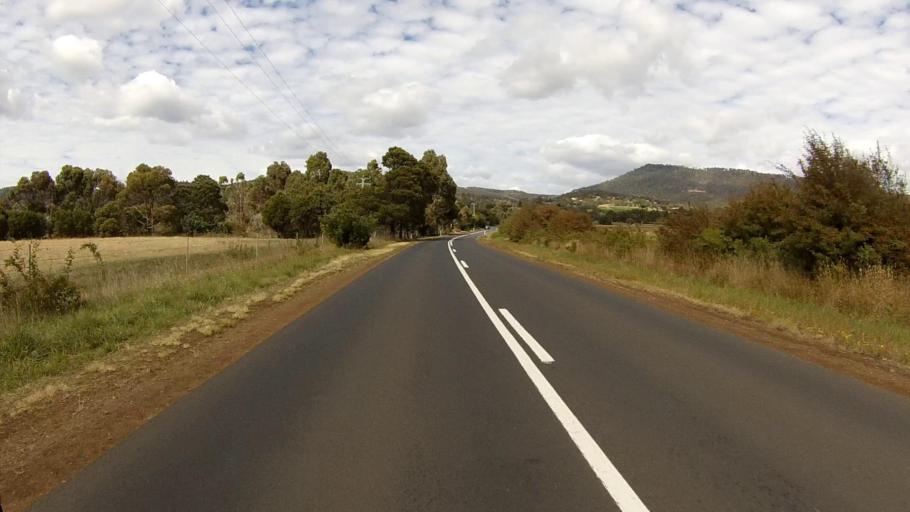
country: AU
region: Tasmania
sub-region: Clarence
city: Cambridge
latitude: -42.7581
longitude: 147.4037
